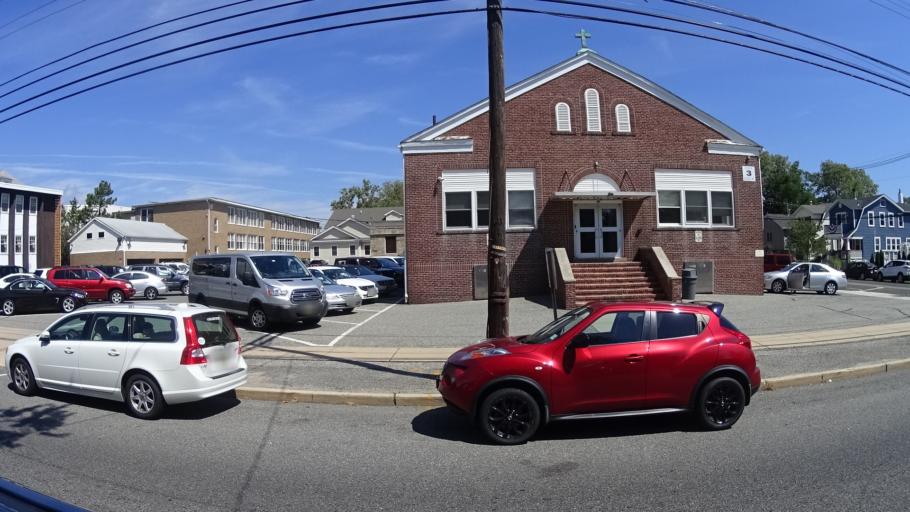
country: US
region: New Jersey
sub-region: Monmouth County
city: Belmar
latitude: 40.1811
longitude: -74.0233
